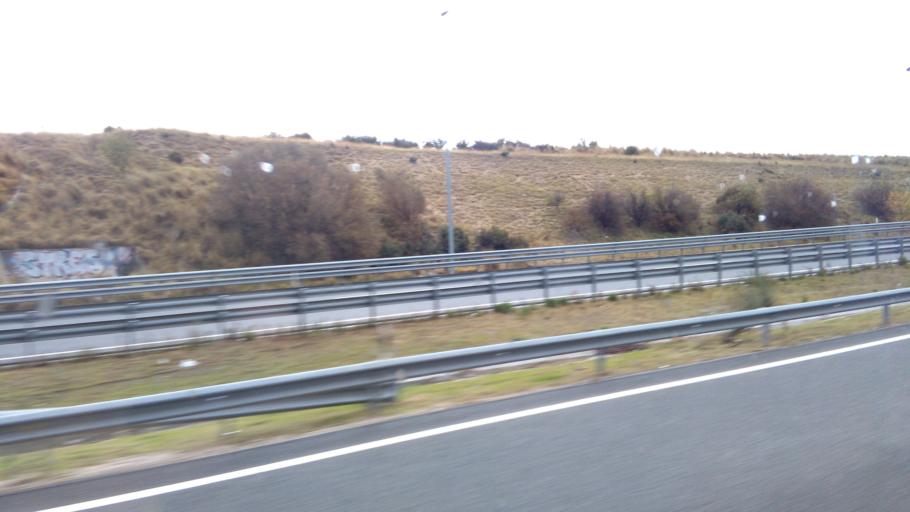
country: ES
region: Madrid
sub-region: Provincia de Madrid
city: Alcorcon
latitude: 40.3400
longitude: -3.7966
